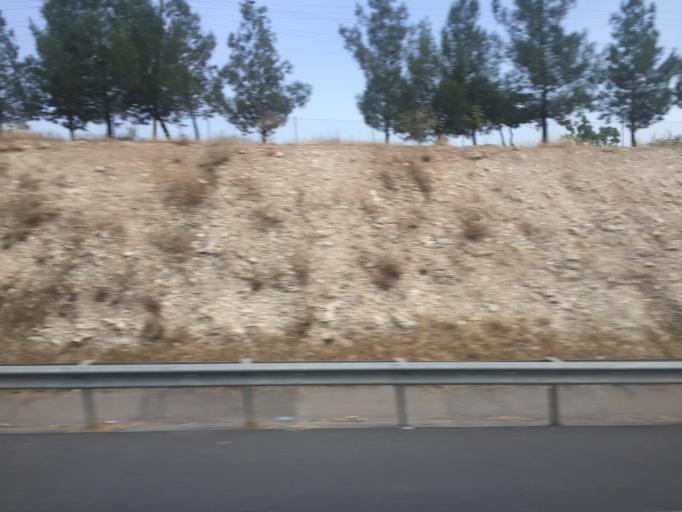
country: TR
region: Sanliurfa
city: Akziyaret
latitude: 37.2664
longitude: 38.8002
